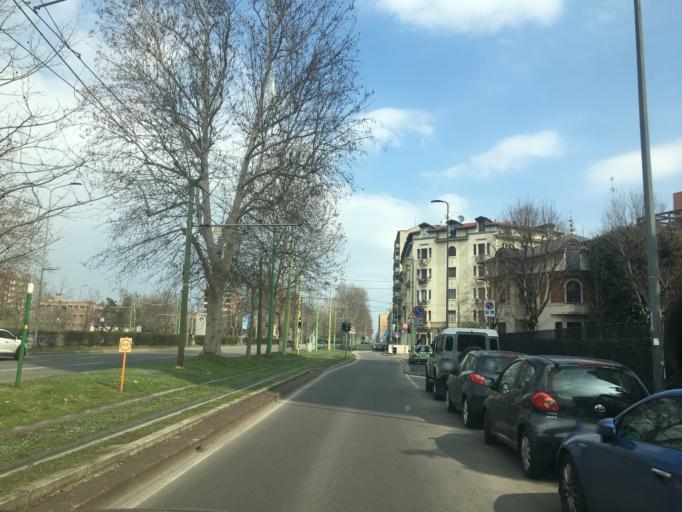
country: IT
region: Lombardy
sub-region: Citta metropolitana di Milano
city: Bresso
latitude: 45.5136
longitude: 9.2050
